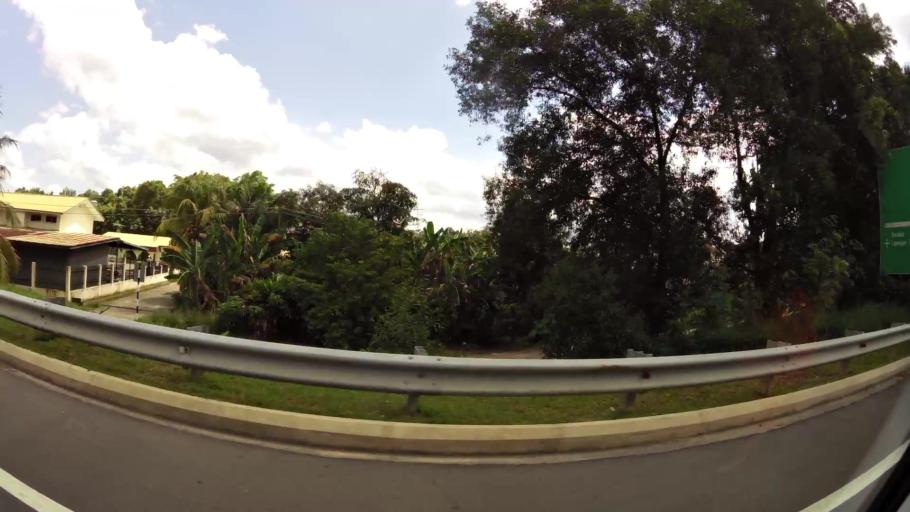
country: BN
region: Brunei and Muara
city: Bandar Seri Begawan
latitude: 4.9456
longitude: 114.9664
